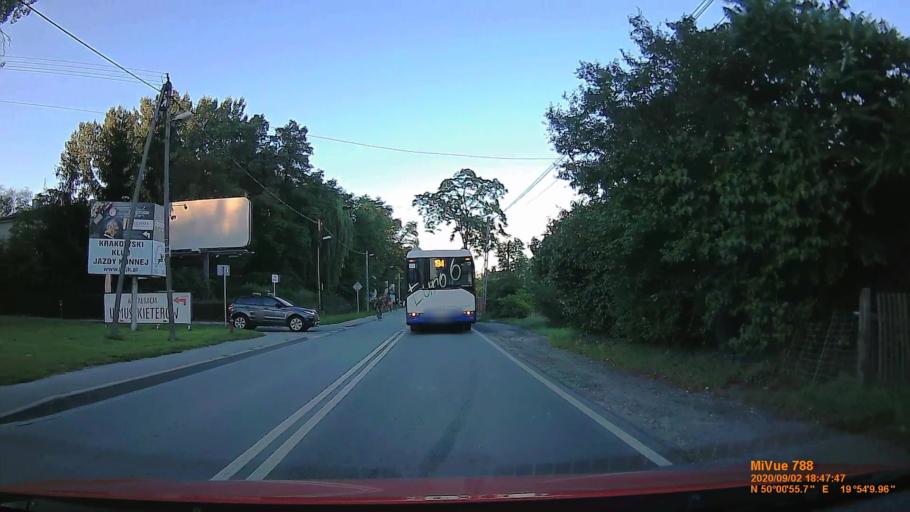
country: PL
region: Lesser Poland Voivodeship
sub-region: Krakow
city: Sidzina
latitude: 50.0157
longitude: 19.9030
